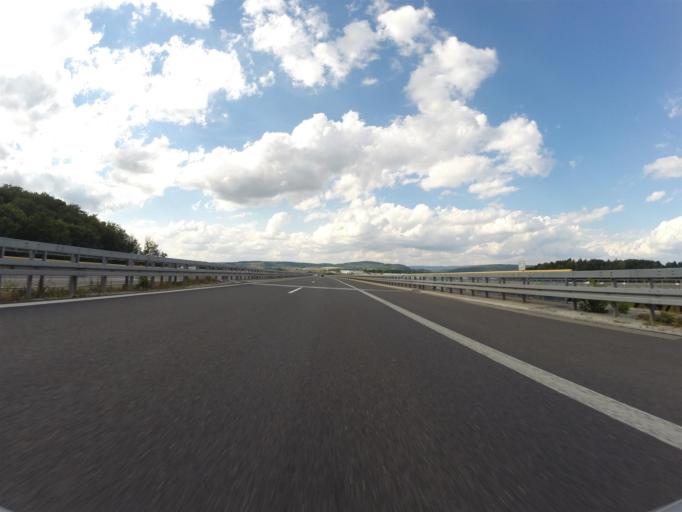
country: DE
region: Bavaria
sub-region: Upper Franconia
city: Rodental
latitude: 50.2771
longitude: 11.0165
